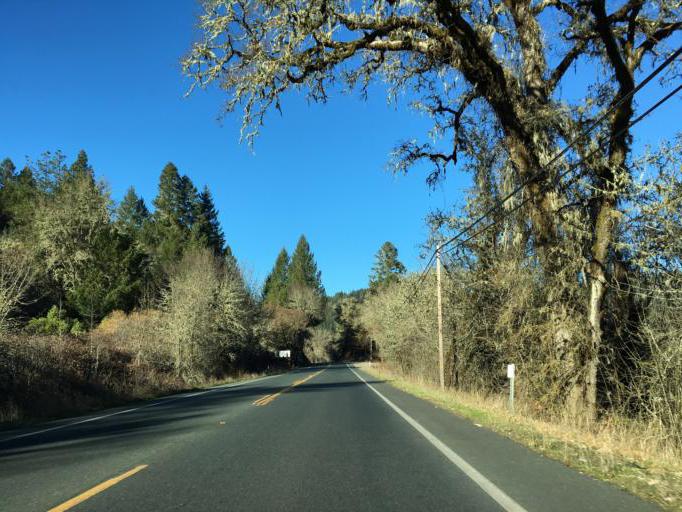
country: US
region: California
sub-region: Mendocino County
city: Brooktrails
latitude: 39.4549
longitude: -123.3484
